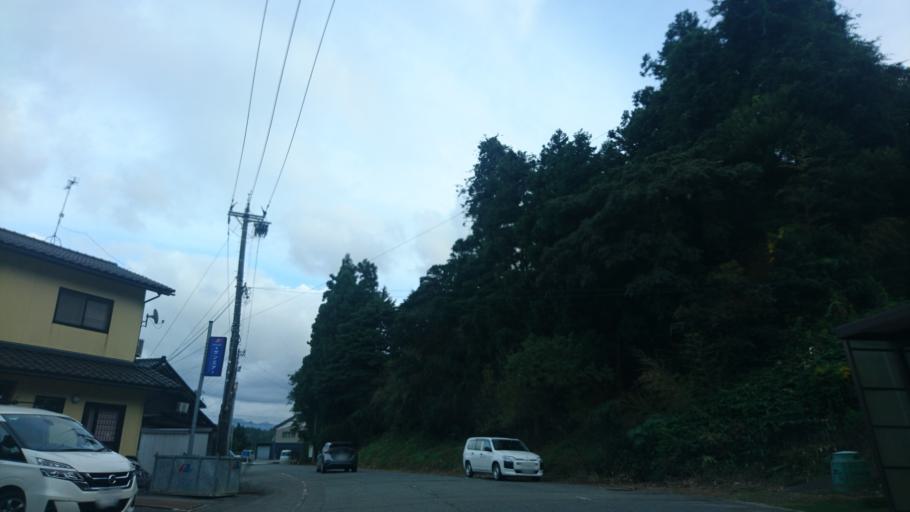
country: JP
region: Fukui
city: Maruoka
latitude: 36.2973
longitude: 136.3184
